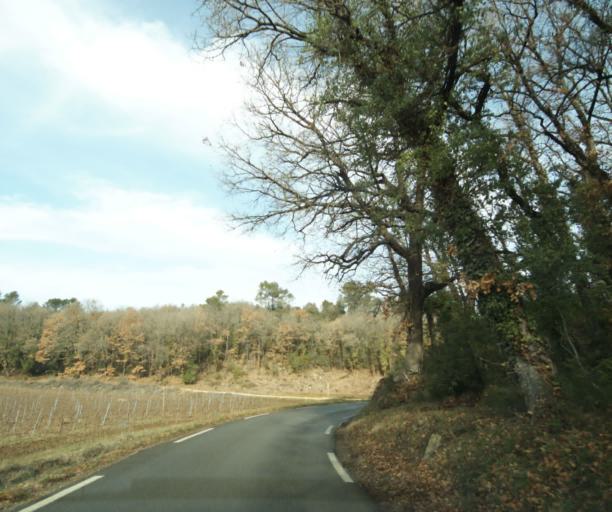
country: FR
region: Provence-Alpes-Cote d'Azur
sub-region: Departement du Var
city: Rougiers
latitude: 43.4116
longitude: 5.8664
